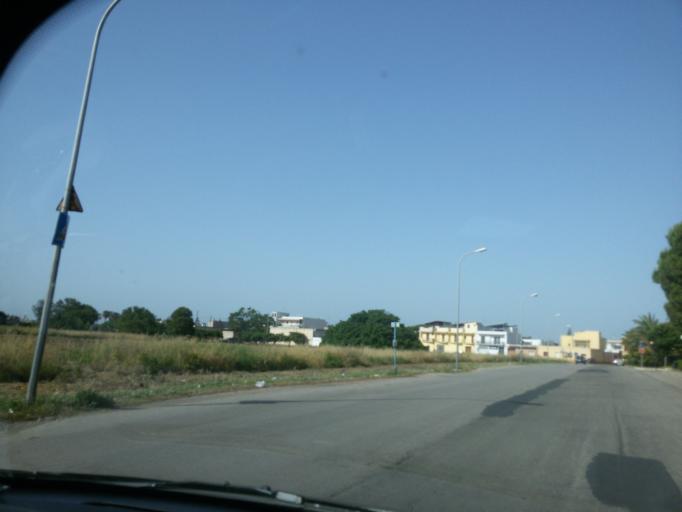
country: IT
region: Apulia
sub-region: Provincia di Brindisi
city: Mesagne
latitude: 40.5516
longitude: 17.8141
